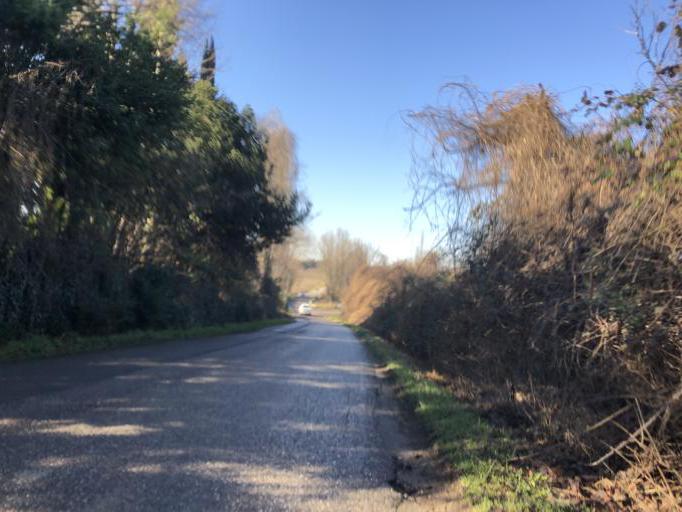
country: IT
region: Veneto
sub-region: Provincia di Verona
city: San Giorgio in Salici
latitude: 45.4275
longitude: 10.7765
